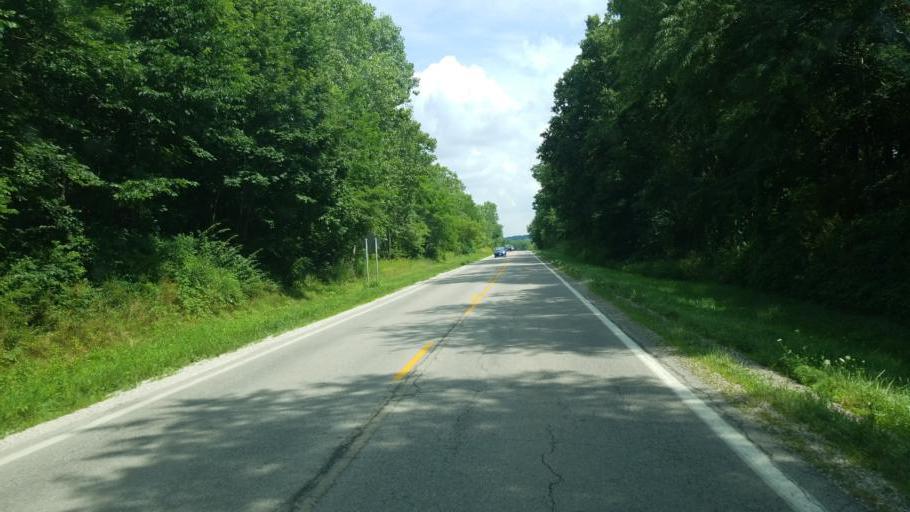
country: US
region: Ohio
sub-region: Sandusky County
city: Bellville
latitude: 40.6167
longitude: -82.4988
